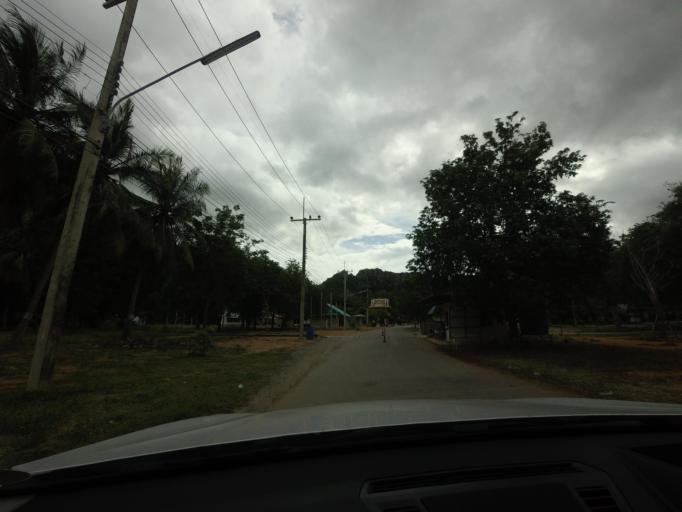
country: TH
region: Prachuap Khiri Khan
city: Sam Roi Yot
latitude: 12.2044
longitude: 100.0084
